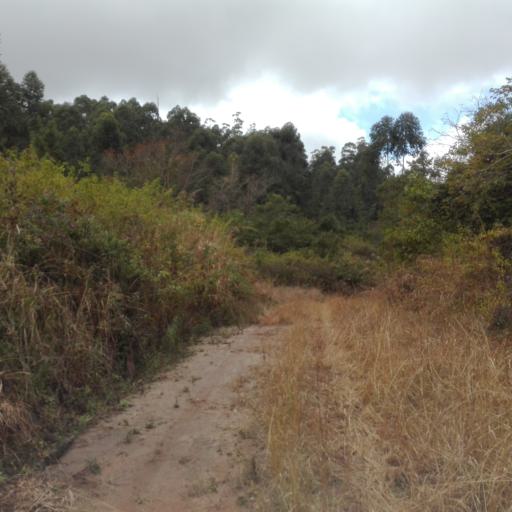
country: ZA
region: Mpumalanga
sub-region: Ehlanzeni District
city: White River
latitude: -25.2440
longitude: 30.9660
